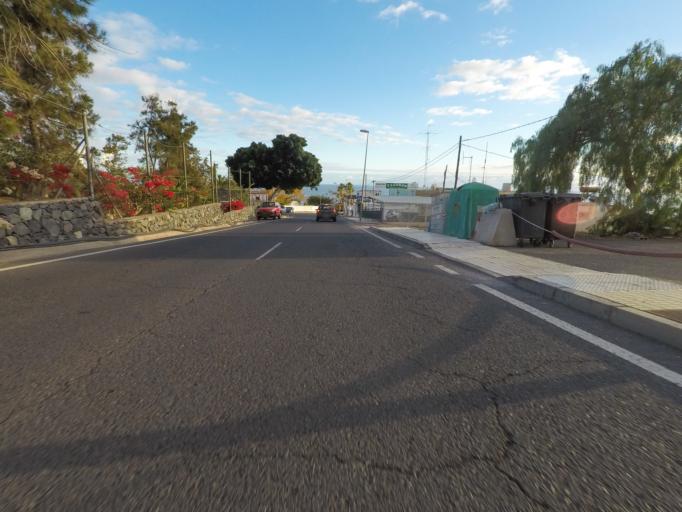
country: ES
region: Canary Islands
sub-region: Provincia de Santa Cruz de Tenerife
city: Alajero
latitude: 28.0317
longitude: -17.1905
